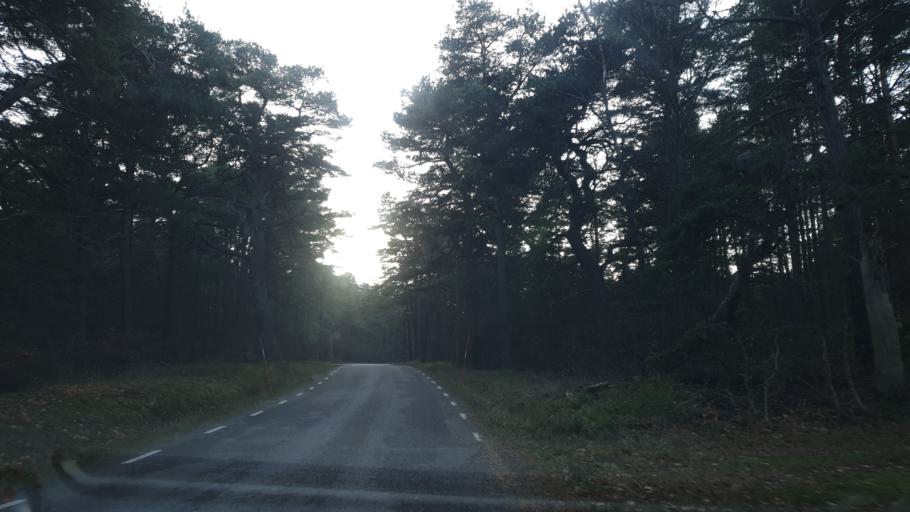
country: SE
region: Kalmar
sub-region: Torsas Kommun
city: Torsas
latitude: 56.2897
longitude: 16.0351
